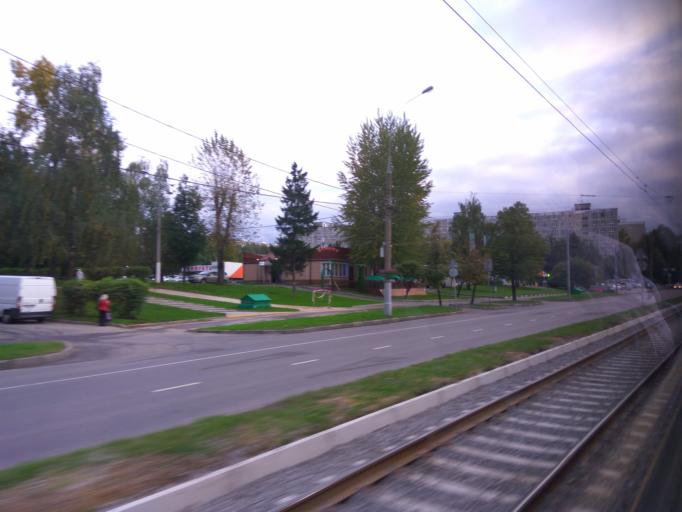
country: RU
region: Moscow
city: Nagornyy
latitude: 55.6301
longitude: 37.6001
